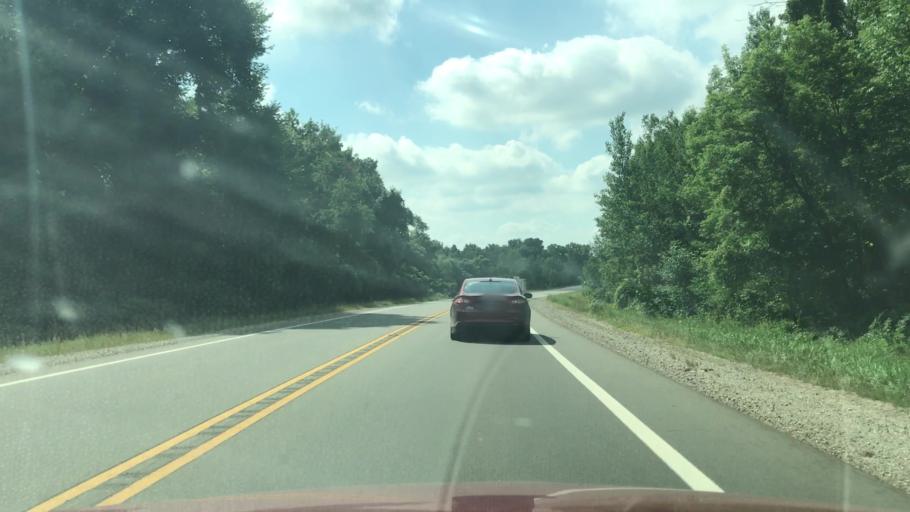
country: US
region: Michigan
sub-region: Kent County
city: Kent City
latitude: 43.1967
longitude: -85.7234
